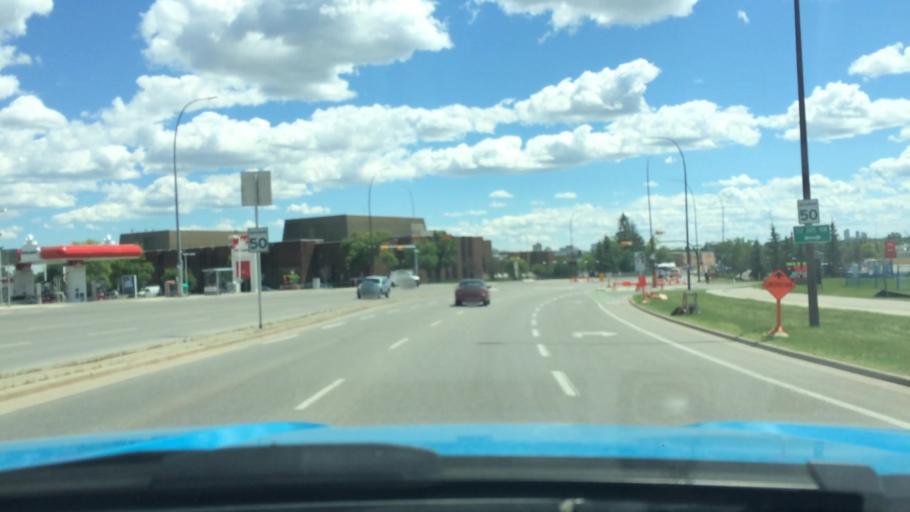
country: CA
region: Alberta
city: Calgary
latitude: 51.1019
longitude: -114.1420
